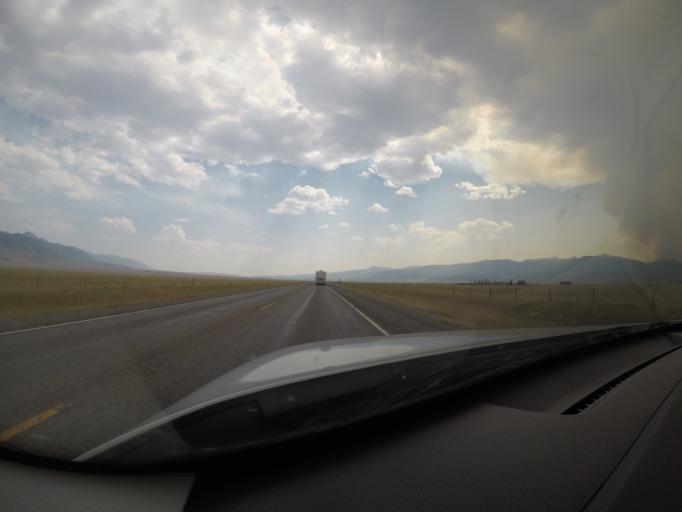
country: US
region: Montana
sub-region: Gallatin County
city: Big Sky
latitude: 45.0638
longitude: -111.6464
